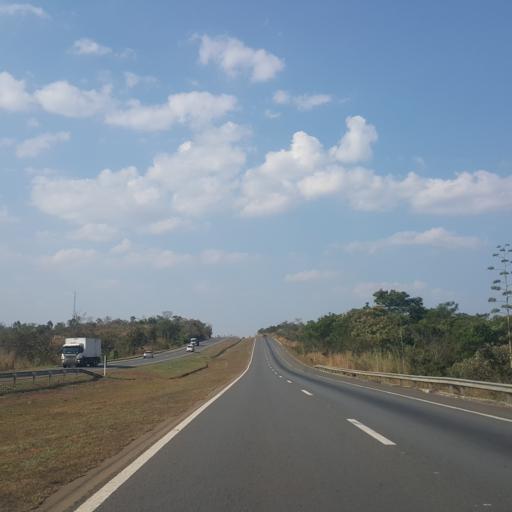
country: BR
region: Goias
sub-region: Abadiania
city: Abadiania
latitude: -16.1691
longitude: -48.6385
